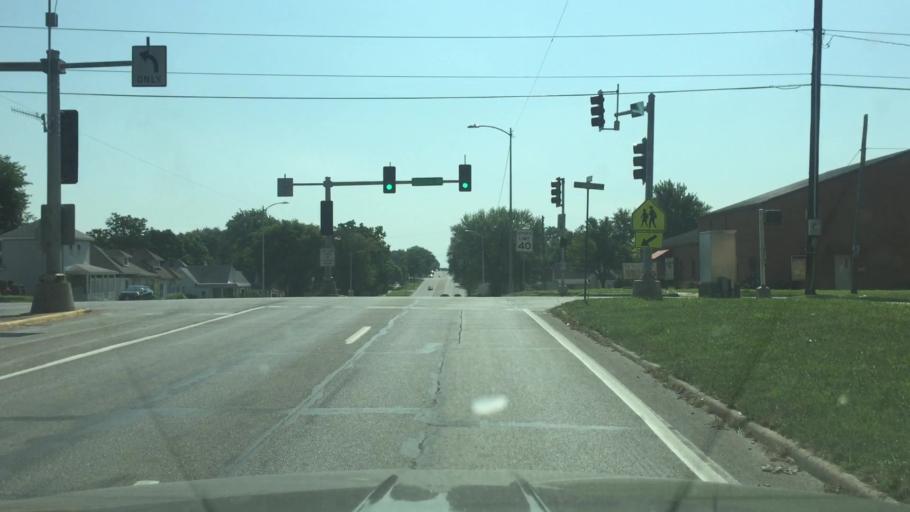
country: US
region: Missouri
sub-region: Pettis County
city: Sedalia
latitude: 38.7036
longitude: -93.2138
